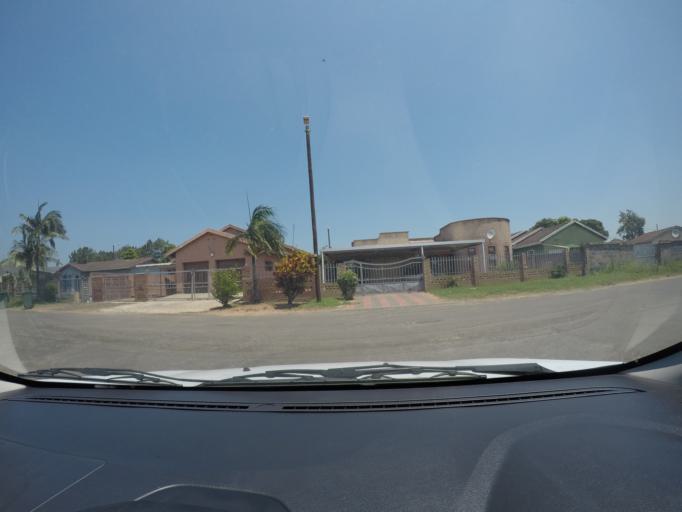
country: ZA
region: KwaZulu-Natal
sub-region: uThungulu District Municipality
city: eSikhawini
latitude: -28.8921
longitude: 31.8865
